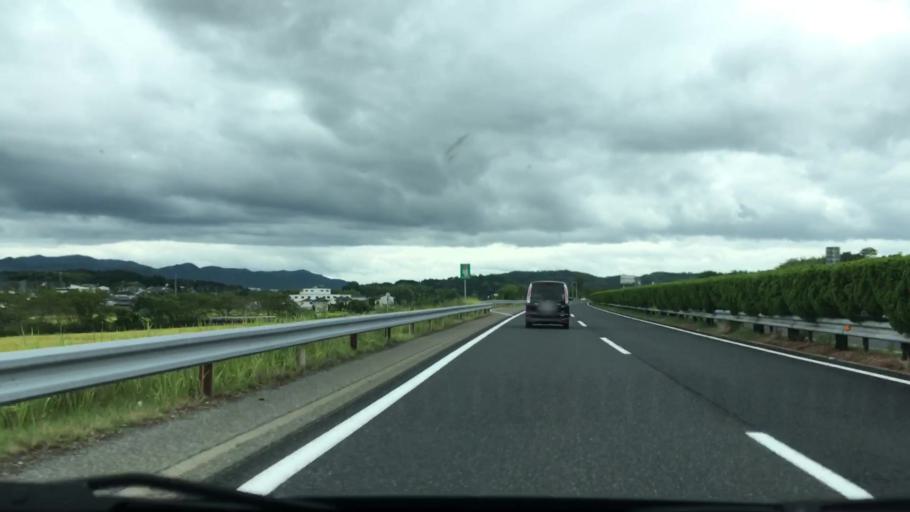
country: JP
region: Okayama
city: Tsuyama
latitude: 35.0455
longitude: 134.0785
